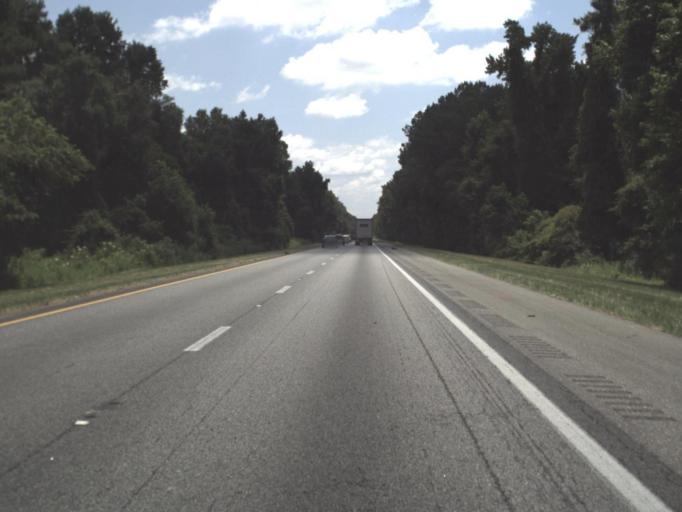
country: US
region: Florida
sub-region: Jefferson County
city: Monticello
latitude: 30.4416
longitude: -83.6660
